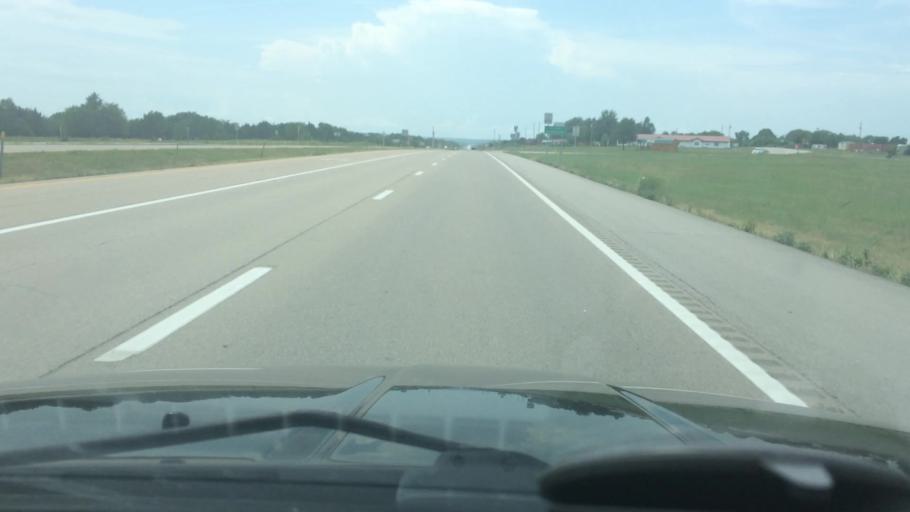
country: US
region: Missouri
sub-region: Polk County
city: Humansville
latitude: 37.7629
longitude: -93.5579
